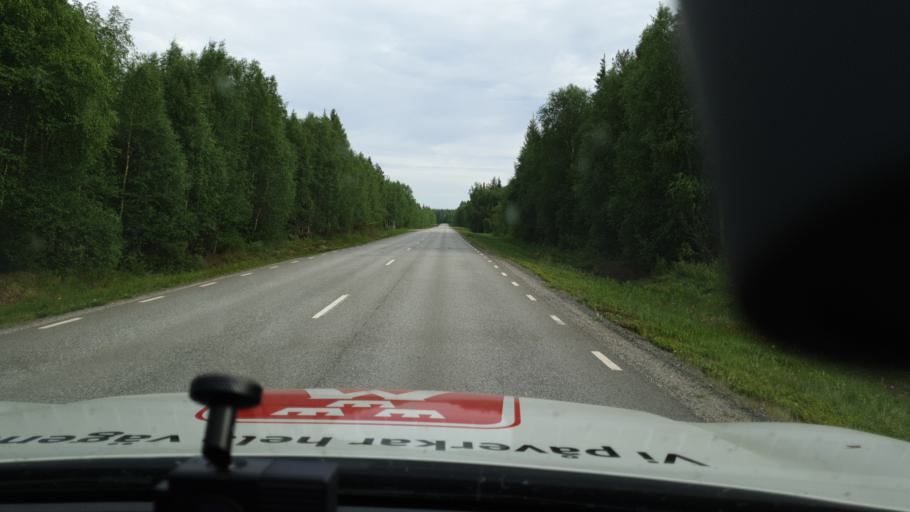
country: SE
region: Vaesterbotten
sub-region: Lycksele Kommun
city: Lycksele
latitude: 64.7044
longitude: 18.6970
